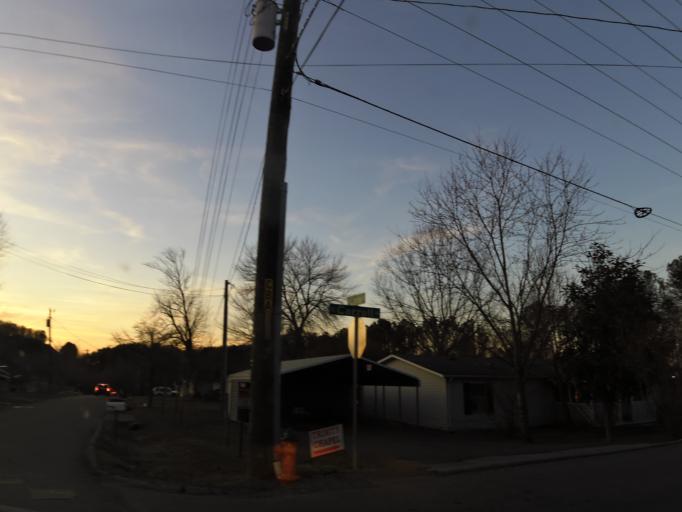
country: US
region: Tennessee
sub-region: Bradley County
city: South Cleveland
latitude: 35.1303
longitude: -84.8810
